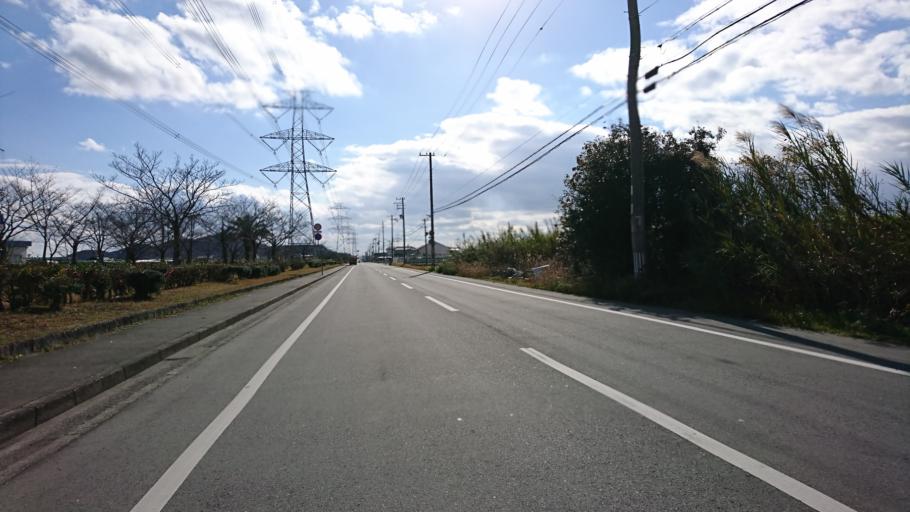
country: JP
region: Hyogo
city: Kakogawacho-honmachi
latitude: 34.8008
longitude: 134.7831
